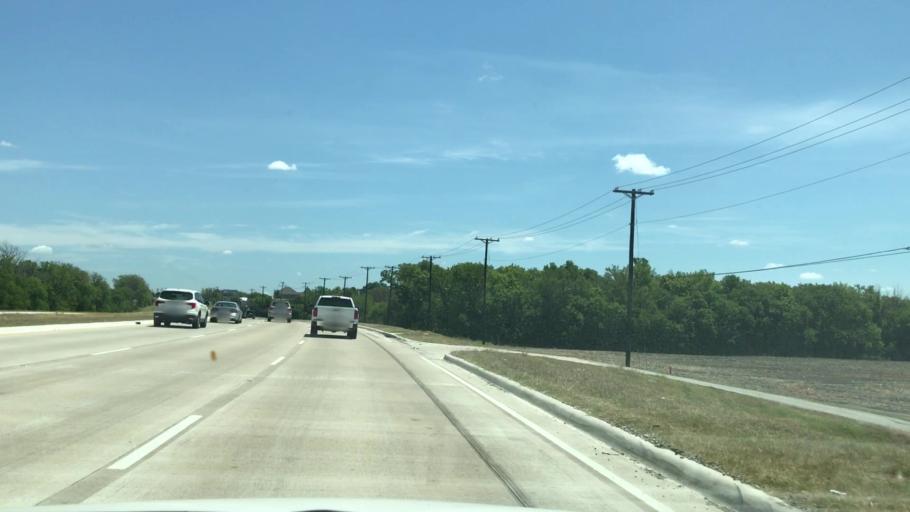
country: US
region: Texas
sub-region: Collin County
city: Lavon
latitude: 33.0216
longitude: -96.4697
